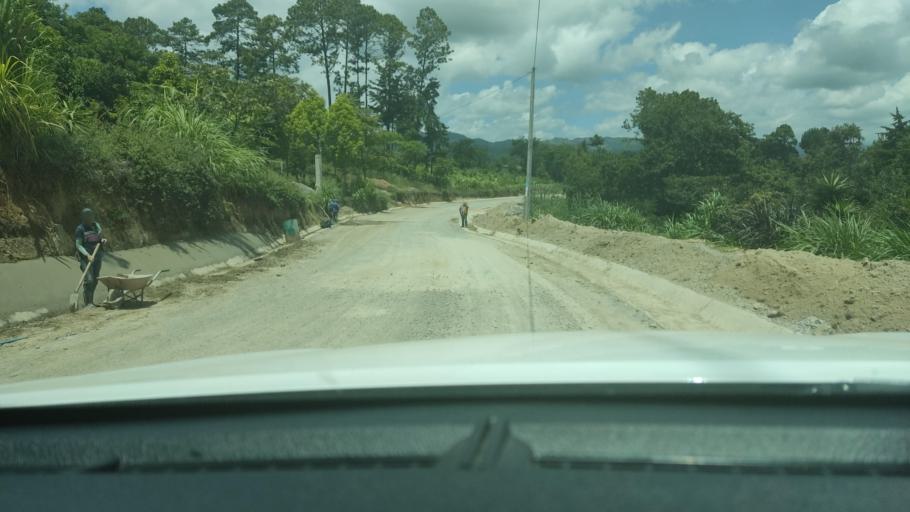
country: GT
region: Chimaltenango
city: San Martin Jilotepeque
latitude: 14.7917
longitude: -90.8062
